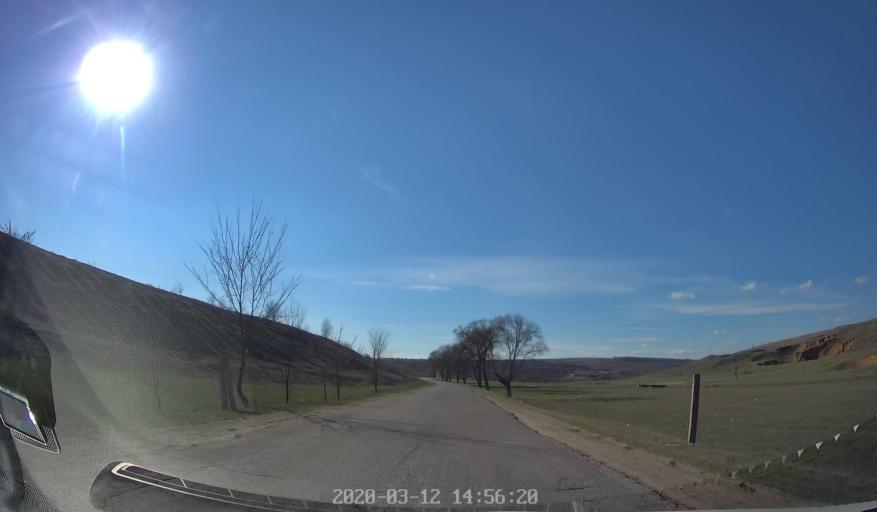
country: MD
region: Telenesti
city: Cocieri
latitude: 47.2249
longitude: 29.0508
